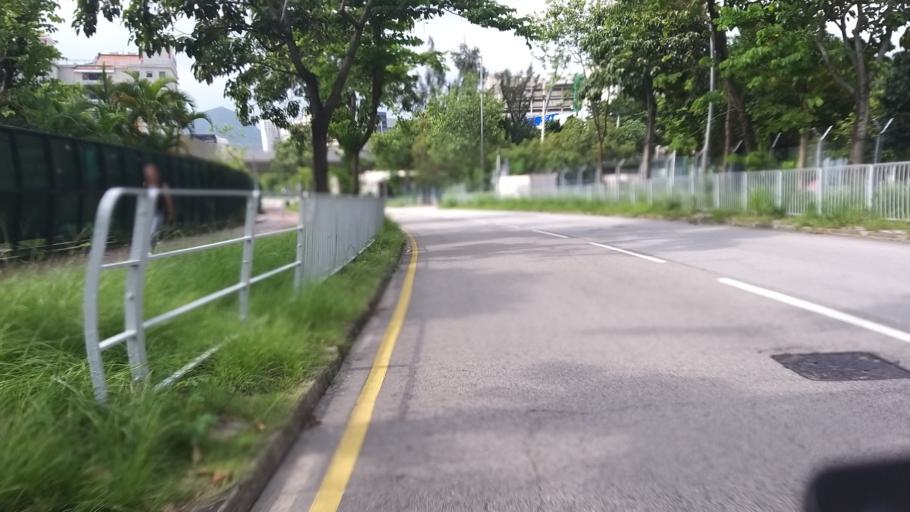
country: HK
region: Tuen Mun
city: Tuen Mun
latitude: 22.4045
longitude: 113.9749
